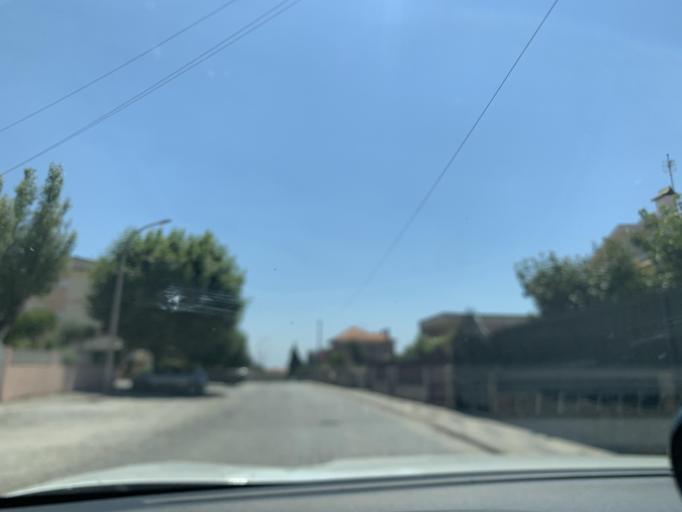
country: PT
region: Viseu
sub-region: Nelas
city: Nelas
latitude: 40.5363
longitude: -7.8474
